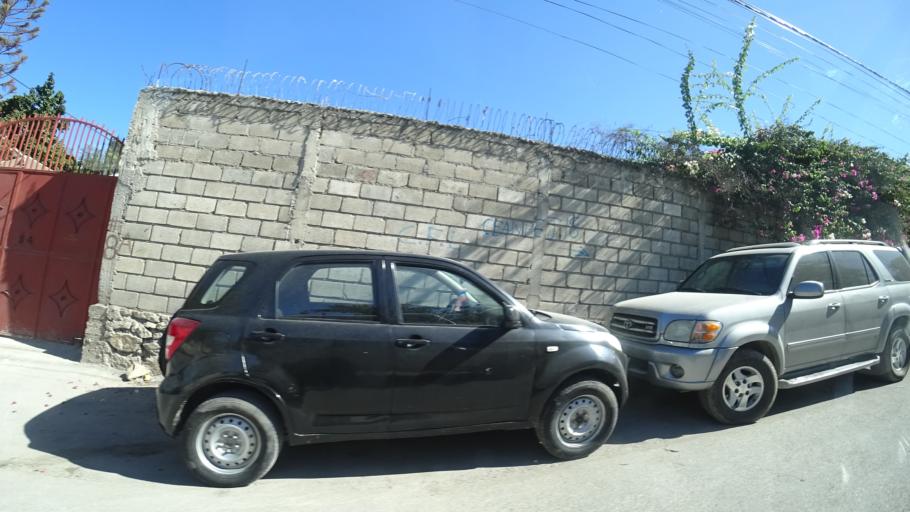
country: HT
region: Ouest
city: Petionville
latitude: 18.5330
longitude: -72.2855
